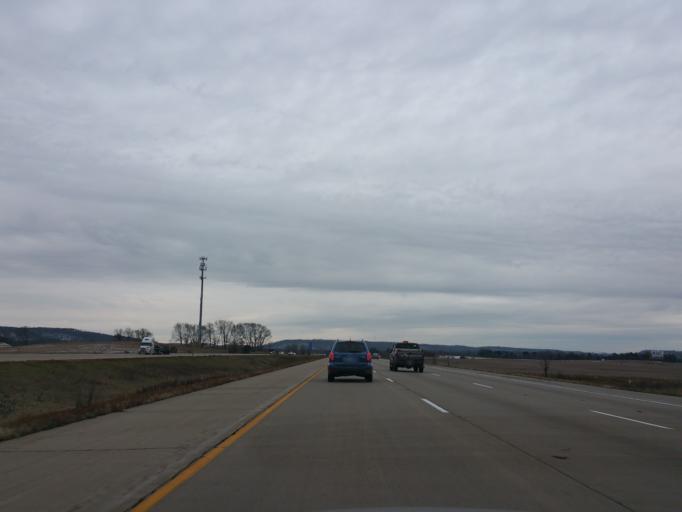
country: US
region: Wisconsin
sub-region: Columbia County
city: Poynette
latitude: 43.4177
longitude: -89.4727
